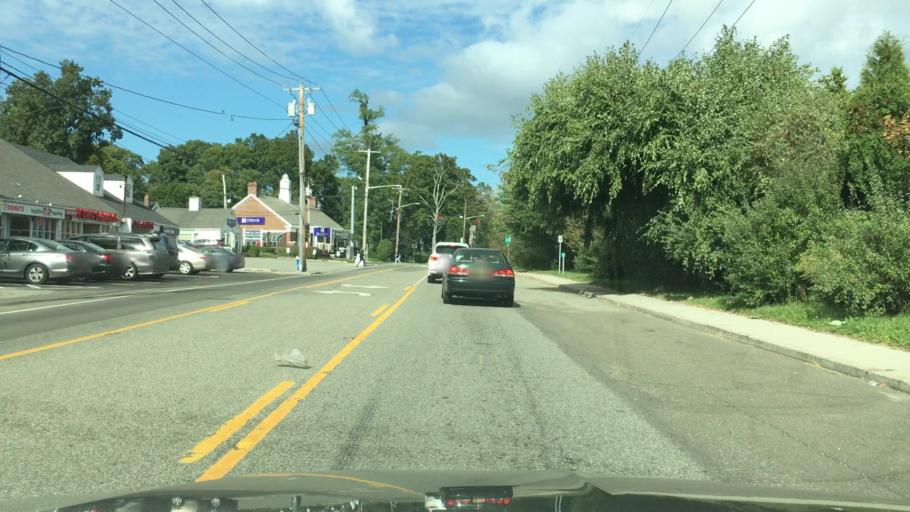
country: US
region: New York
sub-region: Suffolk County
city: Stony Brook
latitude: 40.9202
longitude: -73.1290
